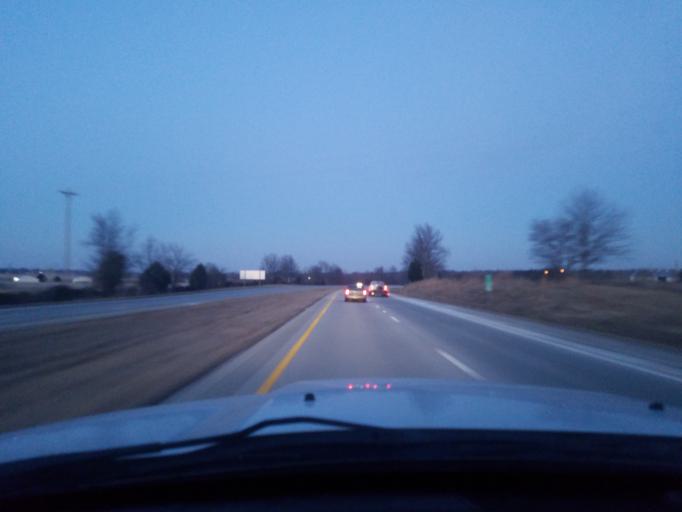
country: US
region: Kentucky
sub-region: Hardin County
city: Elizabethtown
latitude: 37.6457
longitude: -85.9140
